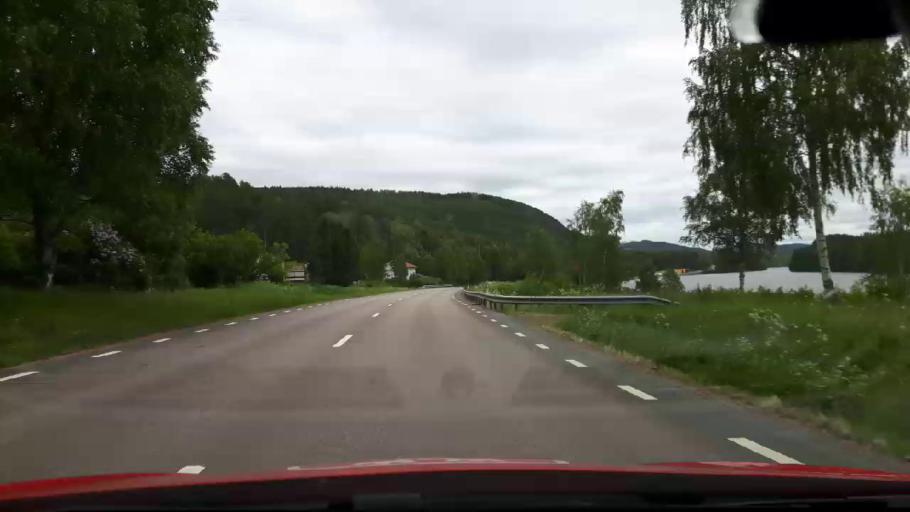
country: SE
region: Jaemtland
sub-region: Ragunda Kommun
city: Hammarstrand
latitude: 63.1451
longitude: 16.3296
